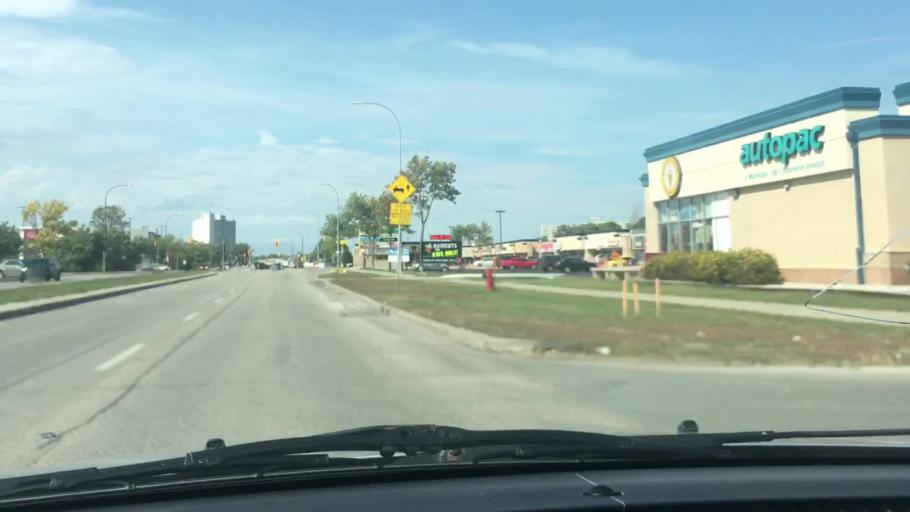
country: CA
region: Manitoba
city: Winnipeg
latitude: 49.8287
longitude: -97.1053
